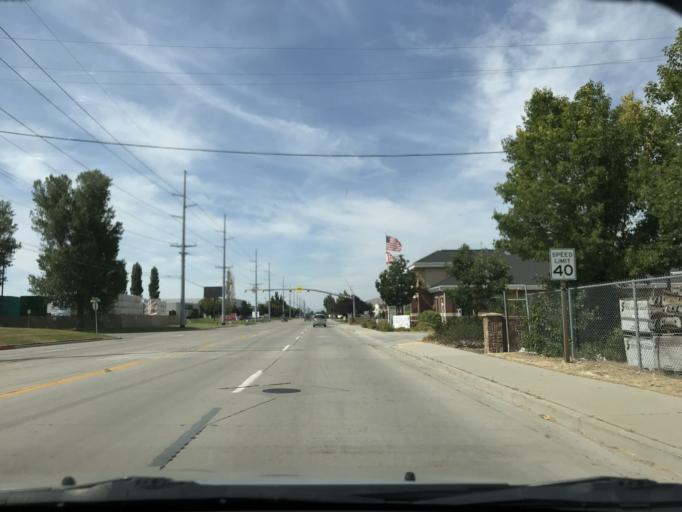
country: US
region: Utah
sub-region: Salt Lake County
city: Centerfield
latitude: 40.7004
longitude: -111.9169
